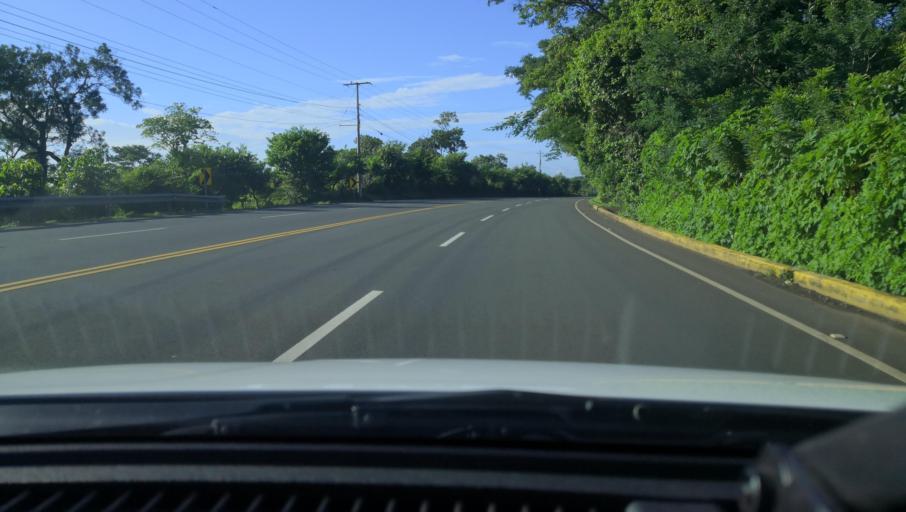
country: NI
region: Granada
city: Nandaime
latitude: 11.7859
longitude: -86.0568
